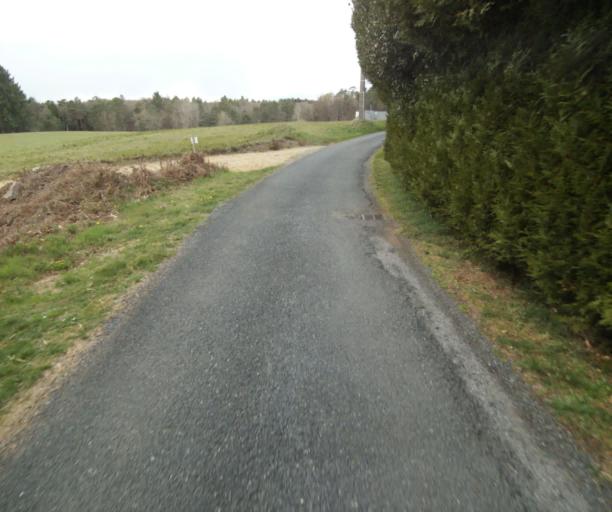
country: FR
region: Limousin
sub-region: Departement de la Correze
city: Correze
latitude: 45.2790
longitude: 1.9434
